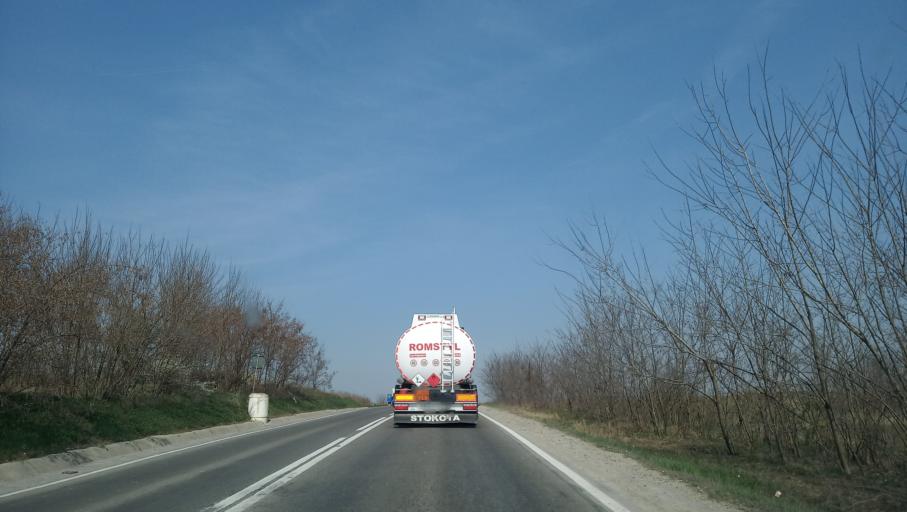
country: RO
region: Alba
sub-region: Oras Teius
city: Teius
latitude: 46.2312
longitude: 23.6832
